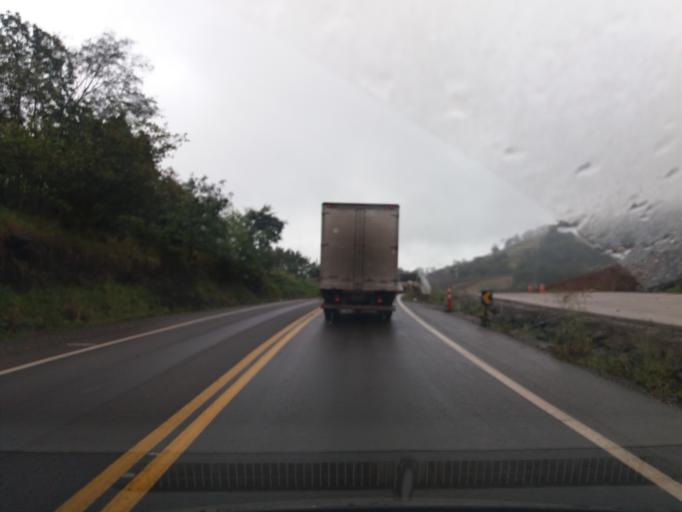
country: BR
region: Parana
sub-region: Realeza
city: Realeza
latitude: -25.4299
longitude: -53.5777
